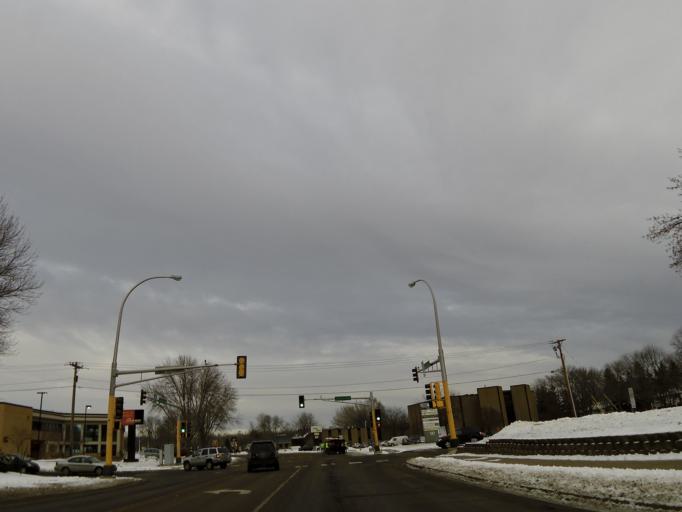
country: US
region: Minnesota
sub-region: Scott County
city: Shakopee
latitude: 44.7970
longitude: -93.5079
